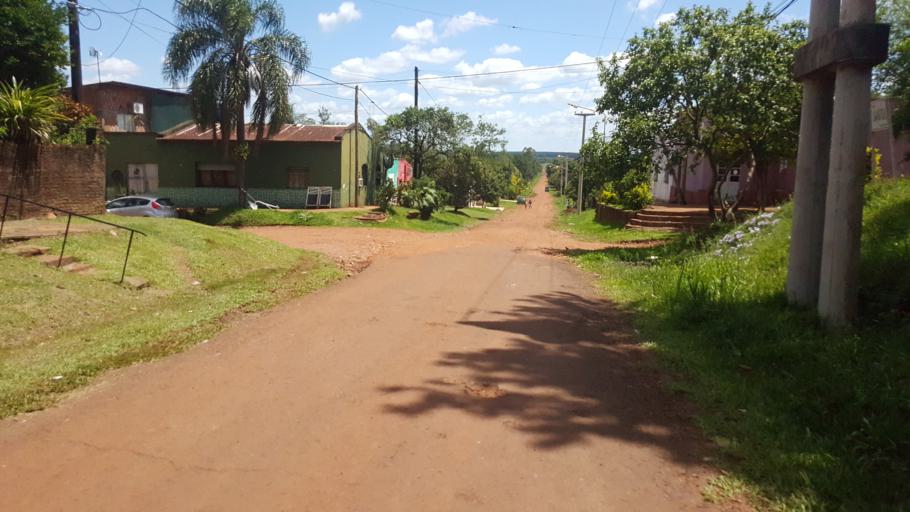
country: AR
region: Corrientes
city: Santo Tome
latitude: -28.5435
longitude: -56.0425
